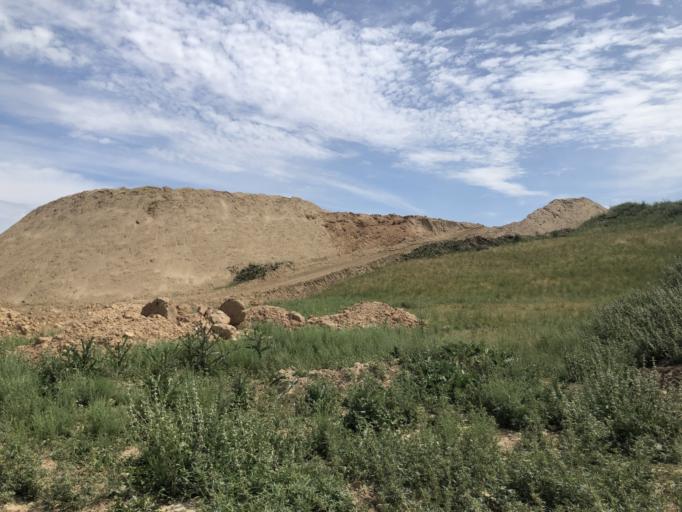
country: KZ
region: Almaty Oblysy
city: Burunday
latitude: 43.2964
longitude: 76.2019
